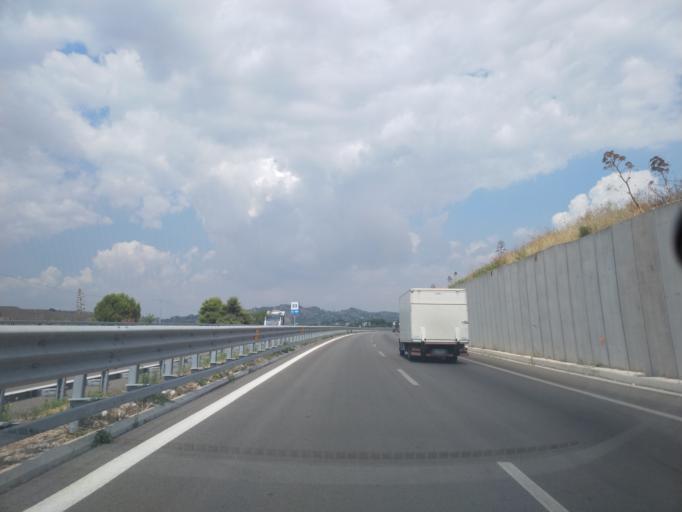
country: IT
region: Sicily
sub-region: Agrigento
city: Grotte
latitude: 37.3685
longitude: 13.7065
